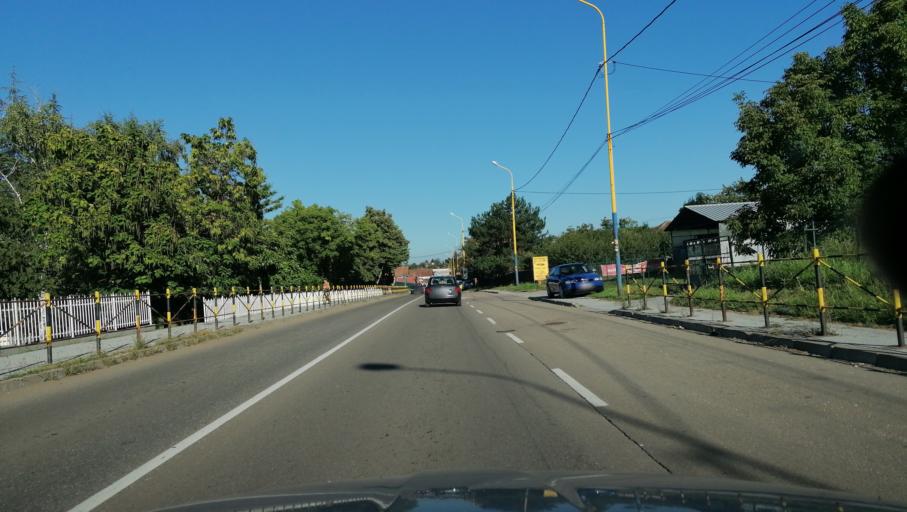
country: RS
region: Central Serbia
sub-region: Sumadijski Okrug
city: Knic
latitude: 43.9271
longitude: 20.7135
